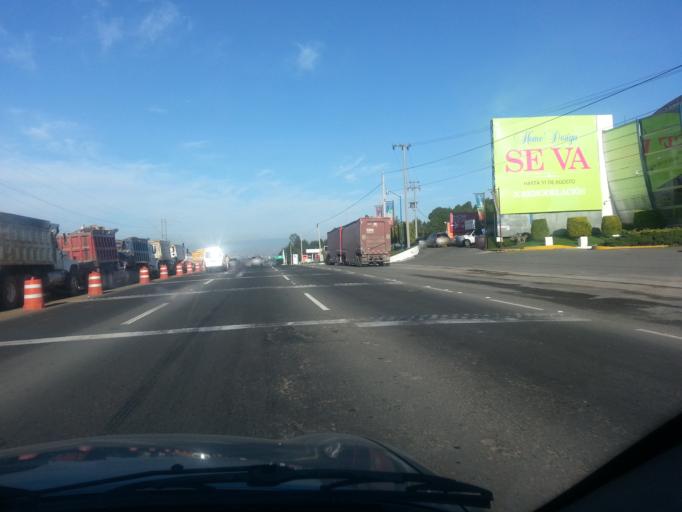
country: MX
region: Mexico
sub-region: Lerma
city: Fraccionamiento y Club de Golf los Encinos
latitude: 19.2824
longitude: -99.4798
